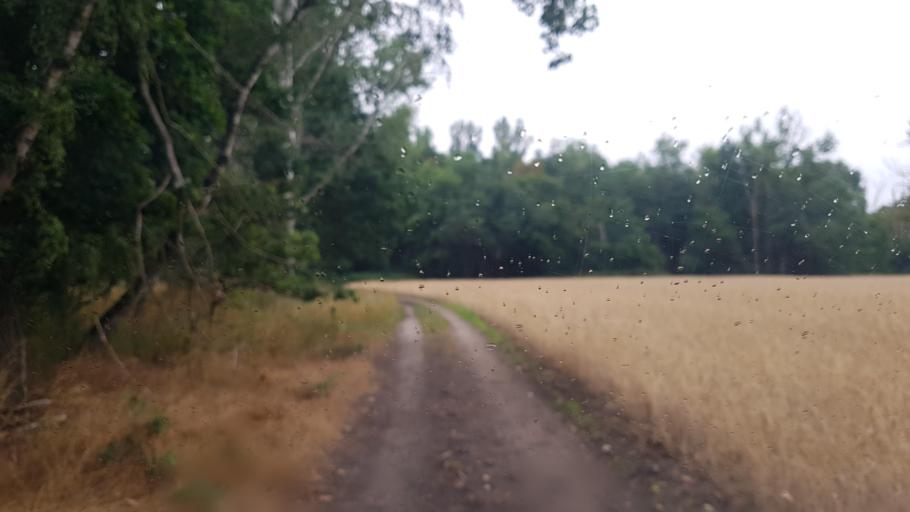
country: DE
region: Brandenburg
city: Ludwigsfelde
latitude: 52.2834
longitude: 13.3032
